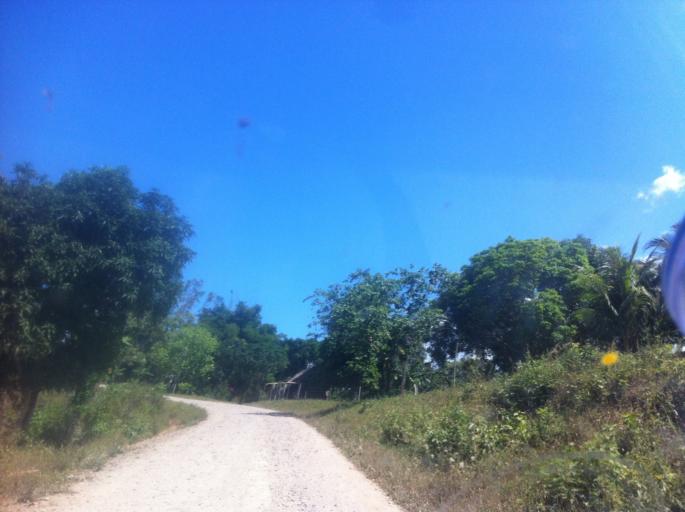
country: NI
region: Rio San Juan
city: San Carlos
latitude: 11.2372
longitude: -84.5252
